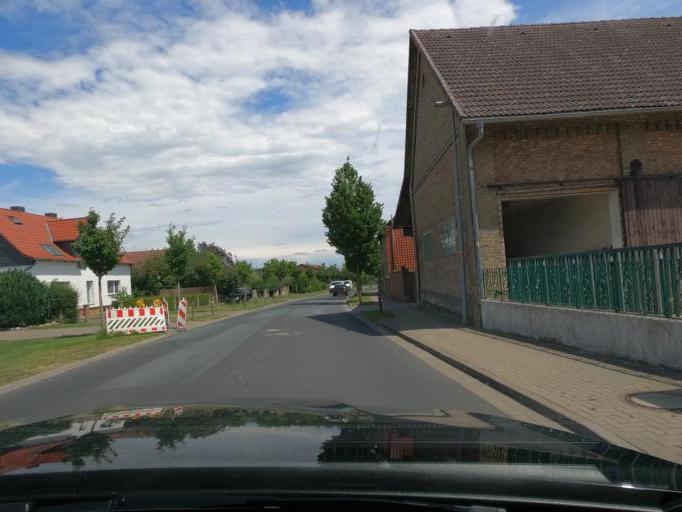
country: DE
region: Lower Saxony
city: Lengede
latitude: 52.1873
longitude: 10.2851
